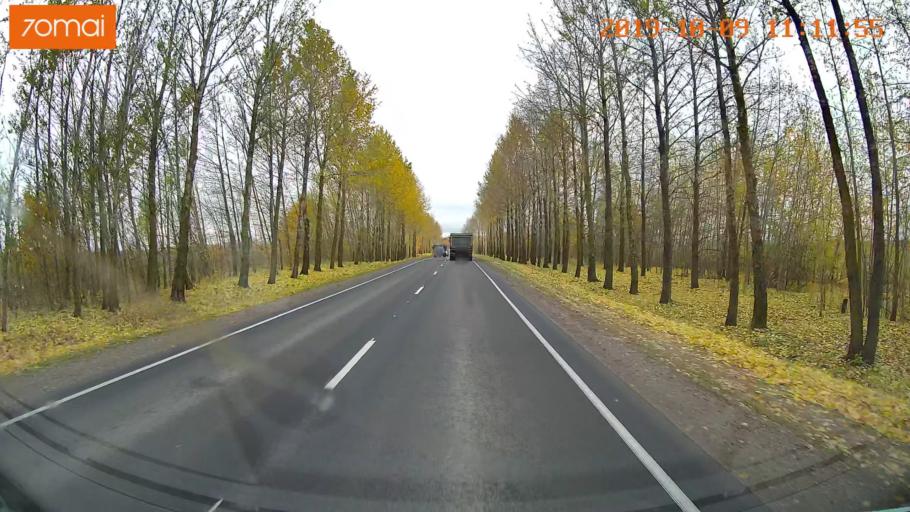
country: RU
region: Vologda
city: Vologda
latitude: 59.1727
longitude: 39.8250
